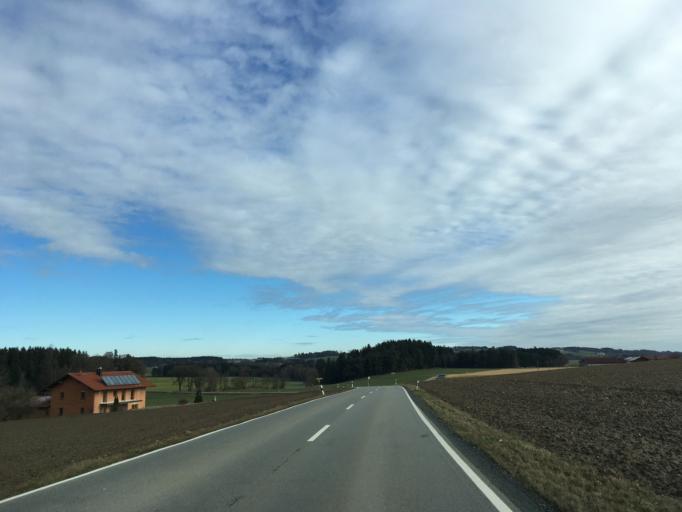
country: DE
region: Bavaria
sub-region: Upper Bavaria
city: Ramsau
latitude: 48.1779
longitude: 12.2547
